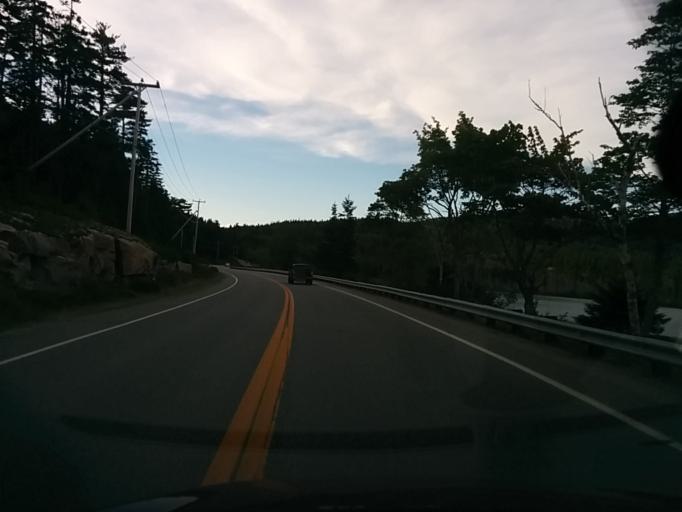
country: US
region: Maine
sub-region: Hancock County
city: Tremont
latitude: 44.3207
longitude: -68.2893
